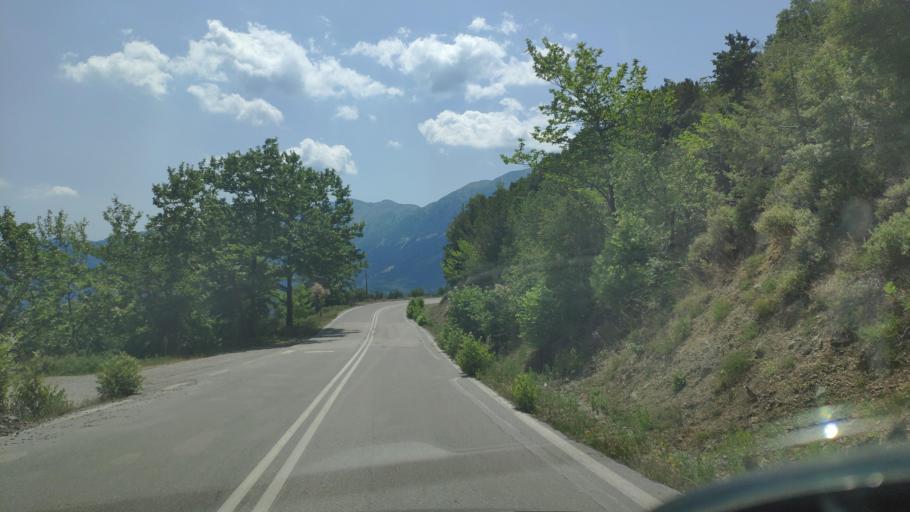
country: GR
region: Thessaly
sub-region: Nomos Kardhitsas
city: Anthiro
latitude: 39.2651
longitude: 21.3478
